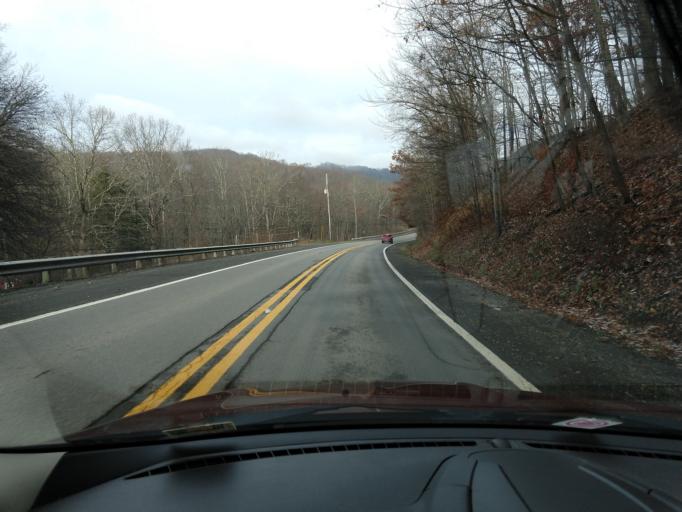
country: US
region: West Virginia
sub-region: Greenbrier County
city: Rainelle
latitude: 38.0344
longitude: -80.7295
